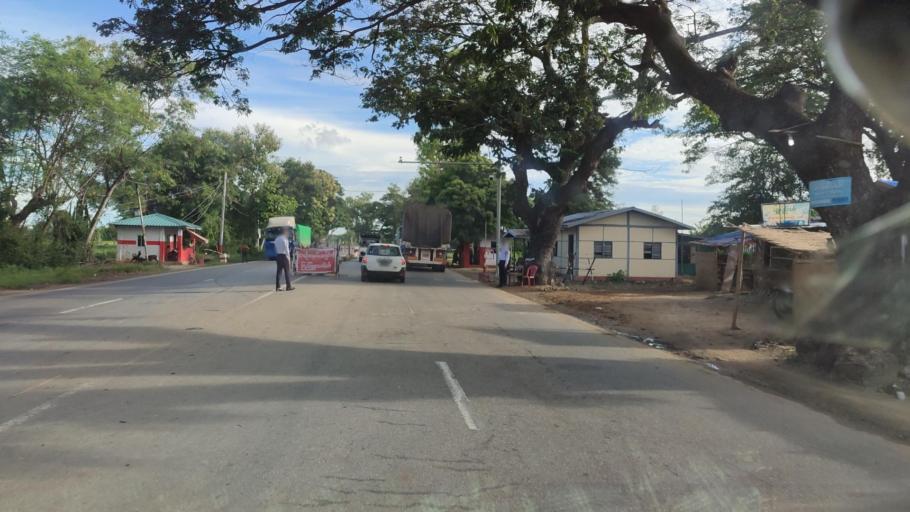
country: MM
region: Mandalay
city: Yamethin
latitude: 20.1736
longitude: 96.1889
